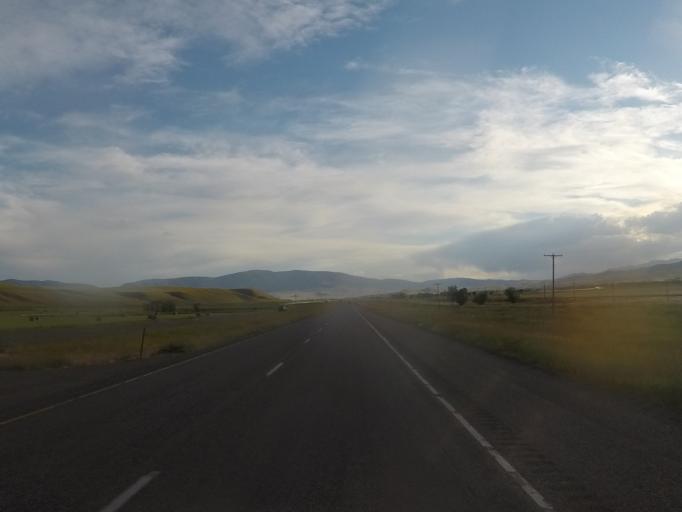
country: US
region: Montana
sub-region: Park County
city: Livingston
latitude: 45.7034
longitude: -110.4638
